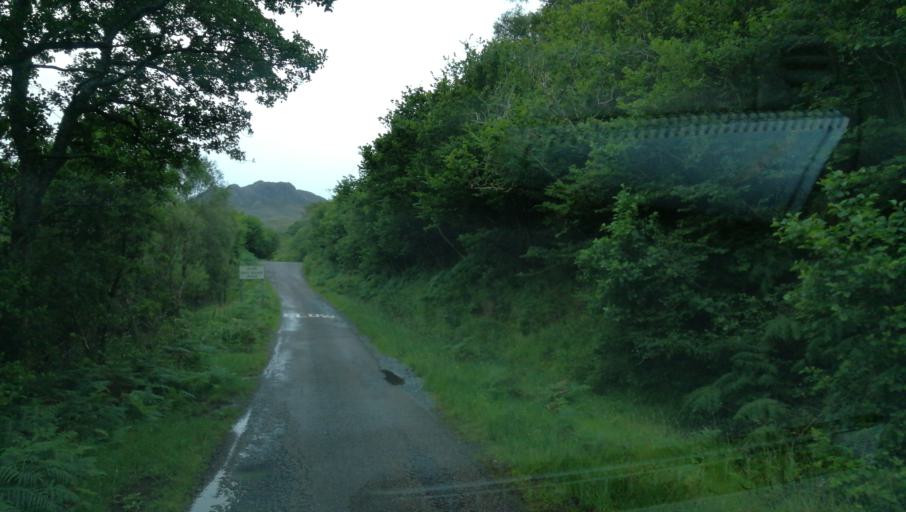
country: GB
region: Scotland
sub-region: Argyll and Bute
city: Isle Of Mull
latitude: 56.7217
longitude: -6.1704
